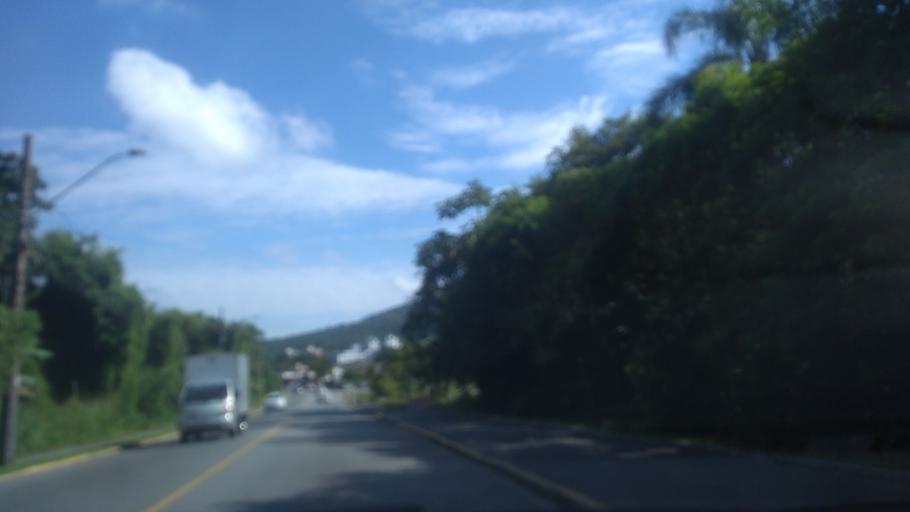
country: BR
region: Santa Catarina
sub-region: Joinville
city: Joinville
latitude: -26.3129
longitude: -48.8284
